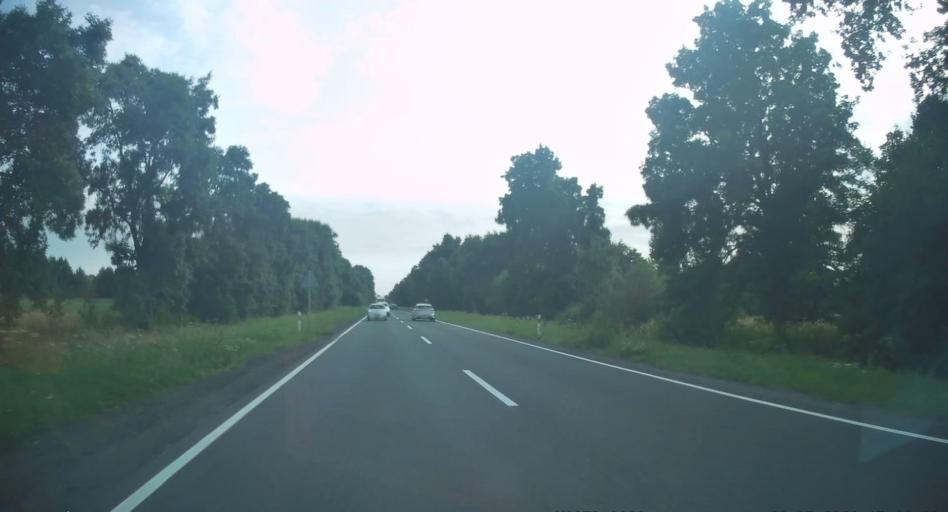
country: PL
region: Silesian Voivodeship
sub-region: Powiat czestochowski
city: Klomnice
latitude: 50.9407
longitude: 19.3892
